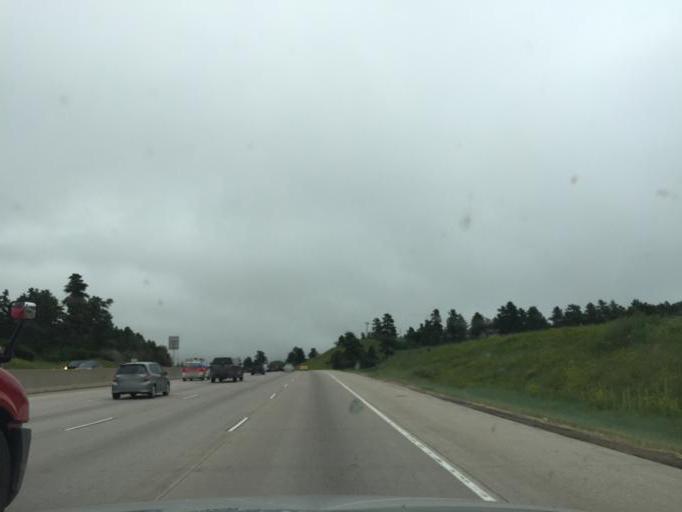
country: US
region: Colorado
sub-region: Douglas County
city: Castle Pines
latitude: 39.4390
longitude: -104.8769
